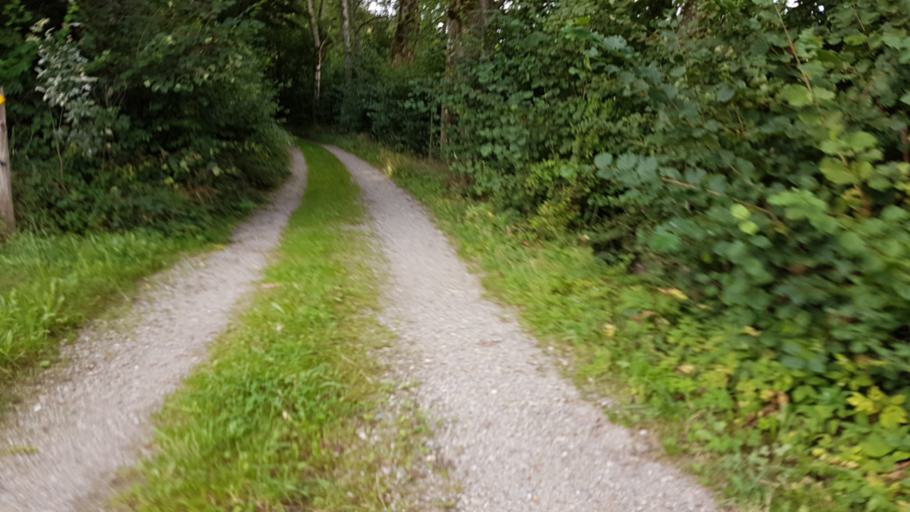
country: CH
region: Bern
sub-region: Bern-Mittelland District
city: Konolfingen
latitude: 46.8628
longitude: 7.6336
